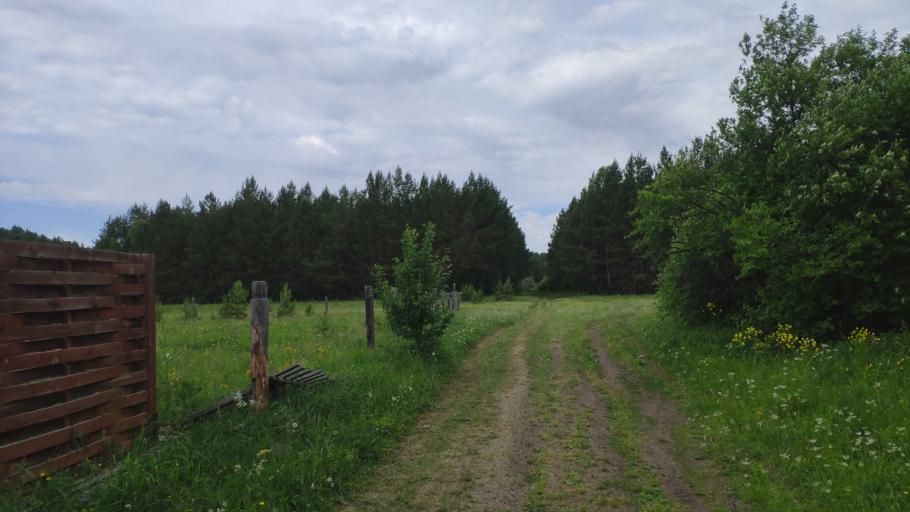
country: RU
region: Bashkortostan
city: Abzakovo
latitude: 53.8170
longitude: 58.6350
